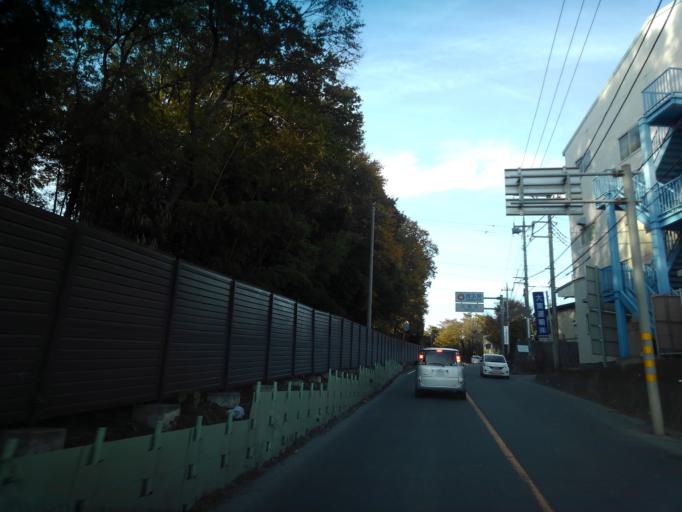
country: JP
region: Tokyo
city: Fussa
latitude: 35.7945
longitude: 139.3436
